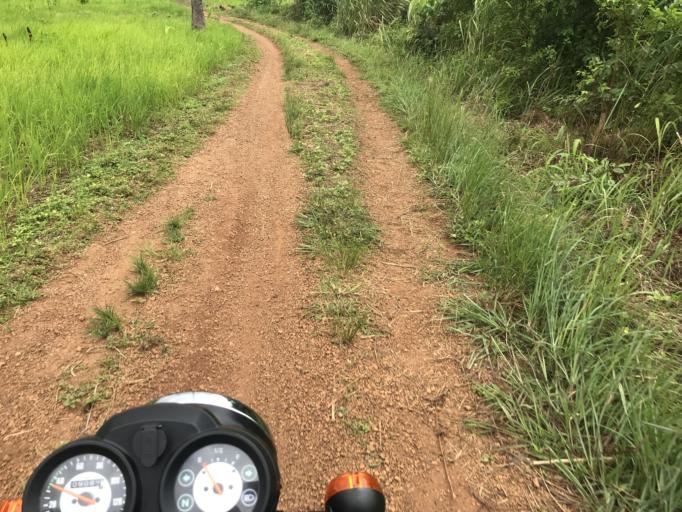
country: SL
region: Eastern Province
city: Buedu
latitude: 8.4771
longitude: -10.3181
